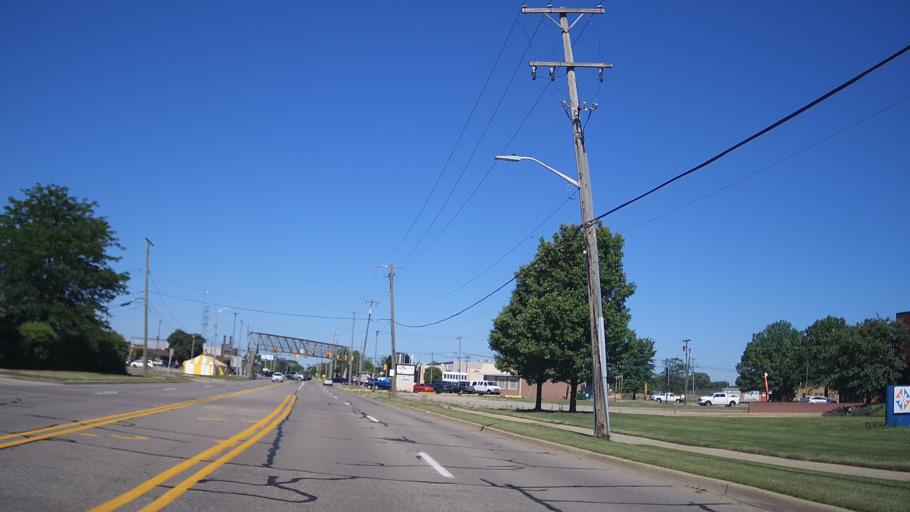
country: US
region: Michigan
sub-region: Macomb County
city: Fraser
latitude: 42.5318
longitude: -82.9384
